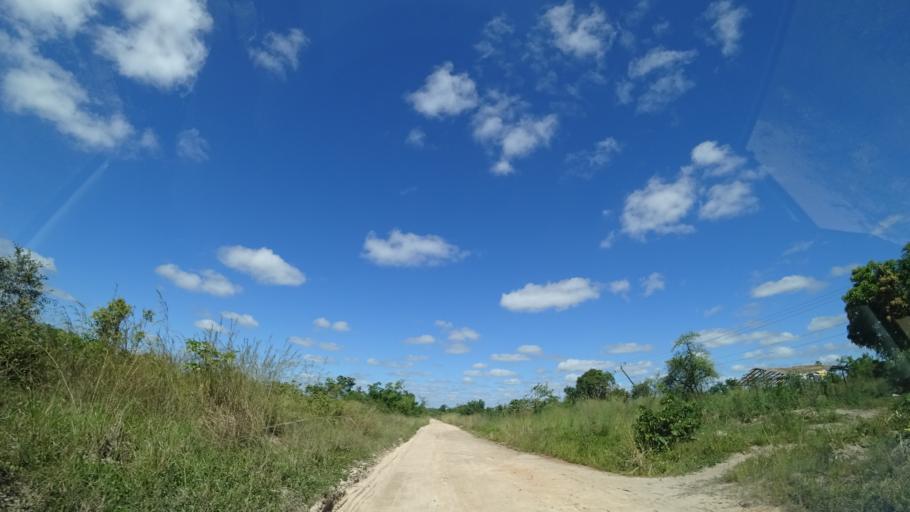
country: MZ
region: Sofala
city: Dondo
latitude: -19.2950
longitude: 34.6904
